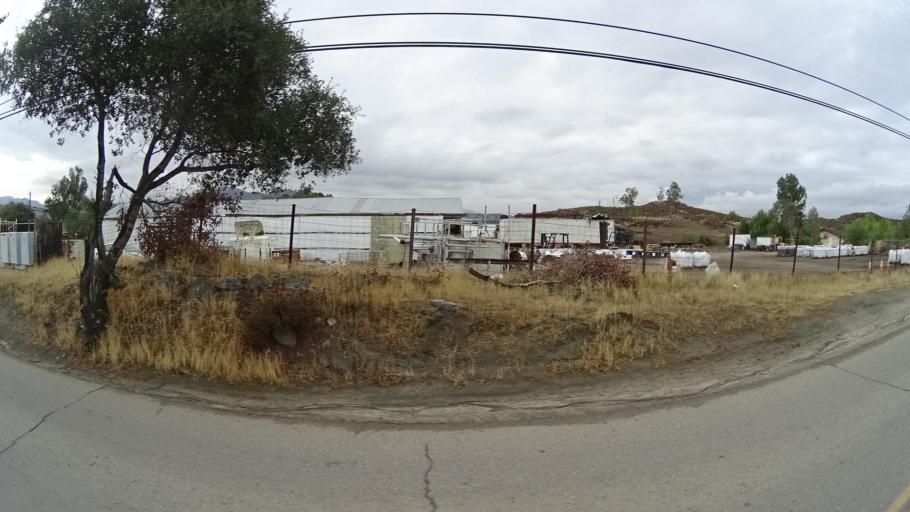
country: MX
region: Baja California
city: Tecate
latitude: 32.5826
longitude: -116.6217
